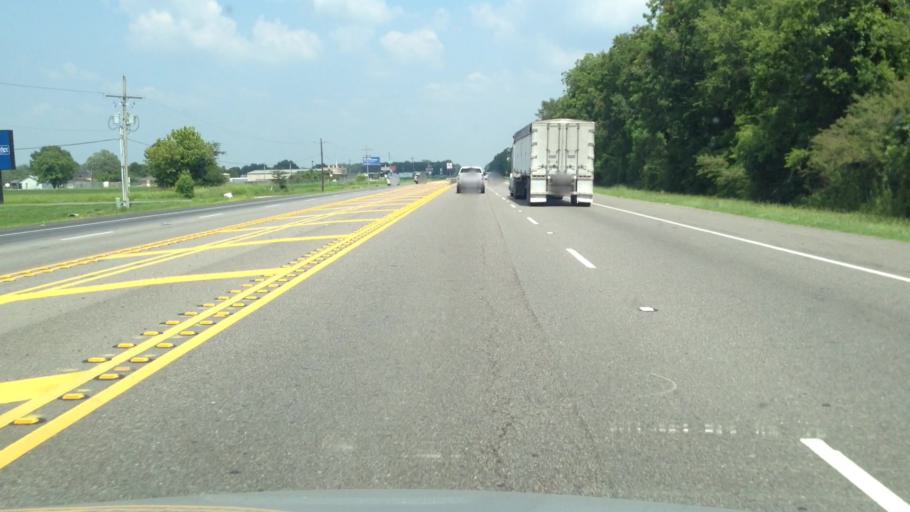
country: US
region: Louisiana
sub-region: Pointe Coupee Parish
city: Livonia
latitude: 30.5546
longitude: -91.5550
